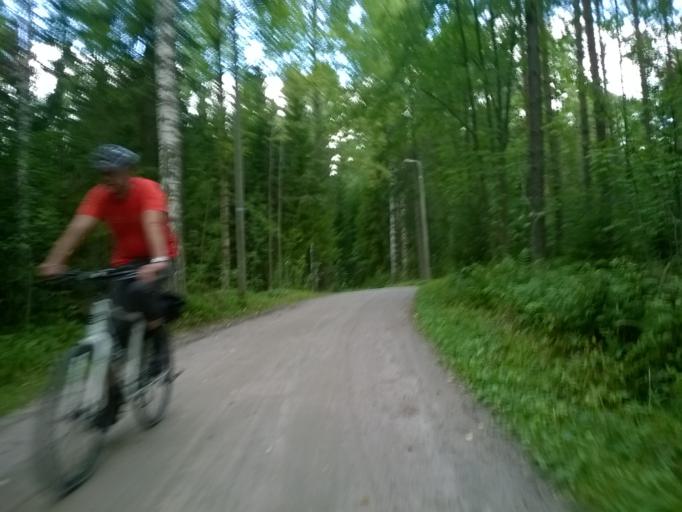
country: FI
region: Uusimaa
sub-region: Helsinki
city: Helsinki
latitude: 60.2612
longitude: 24.9089
